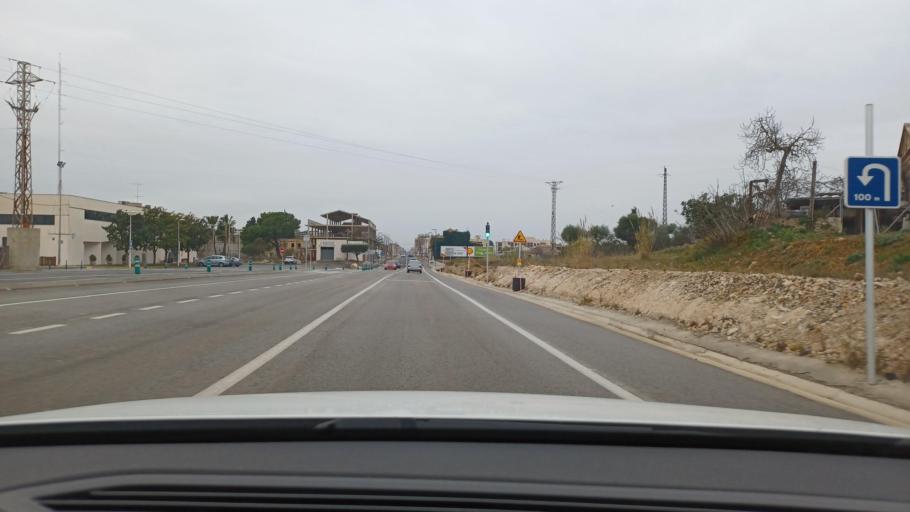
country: ES
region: Catalonia
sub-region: Provincia de Tarragona
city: Camarles
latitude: 40.7467
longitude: 0.6208
